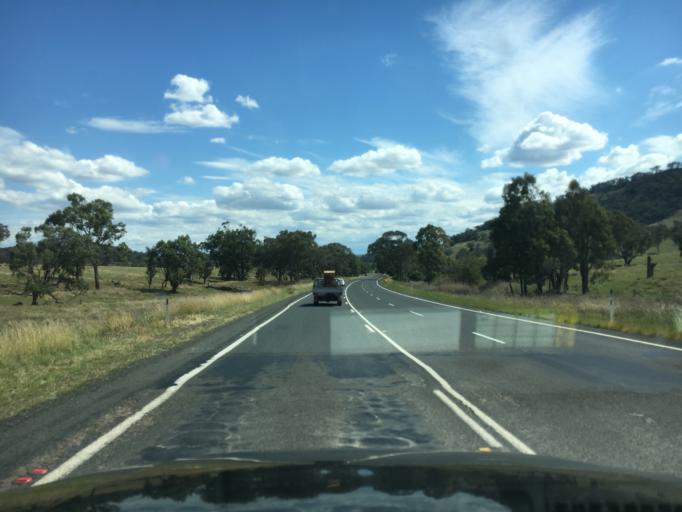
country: AU
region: New South Wales
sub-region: Liverpool Plains
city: Quirindi
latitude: -31.5092
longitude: 150.8589
